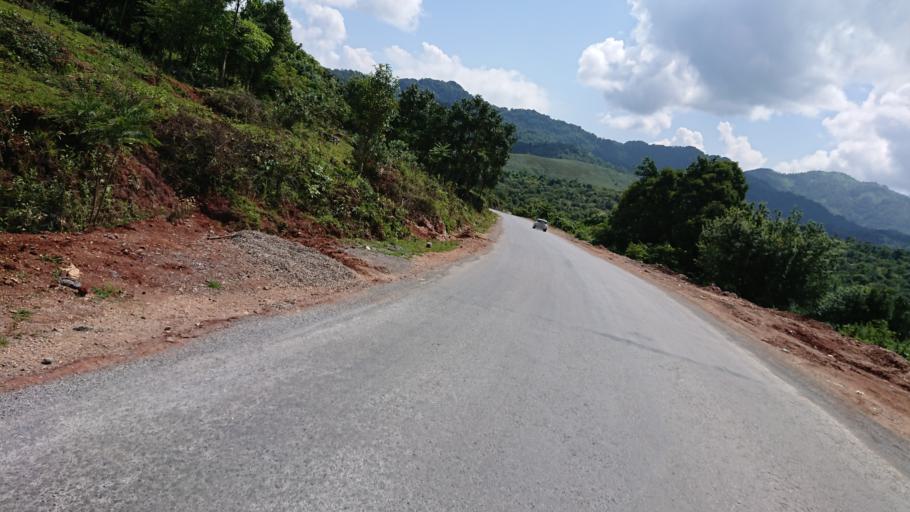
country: MM
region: Shan
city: Taunggyi
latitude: 20.8148
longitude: 97.3295
